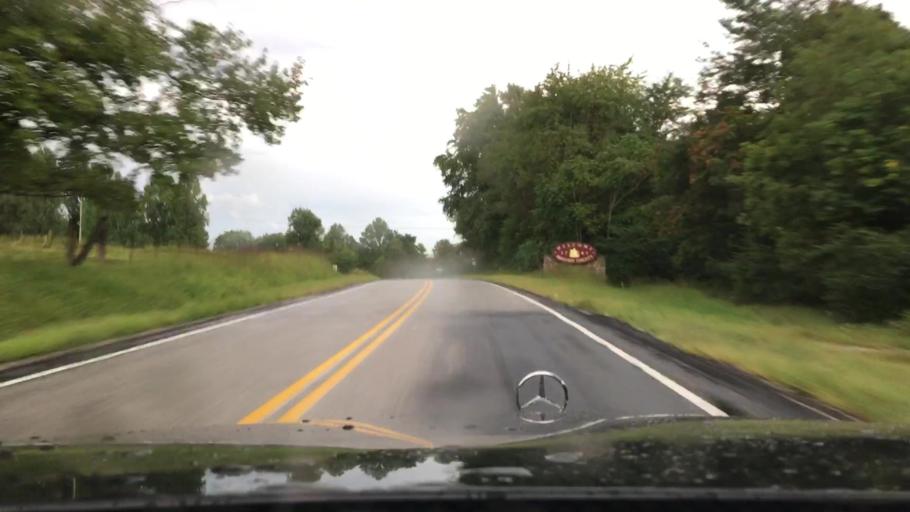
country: US
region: Virginia
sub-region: Amherst County
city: Amherst
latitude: 37.7000
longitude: -79.0290
